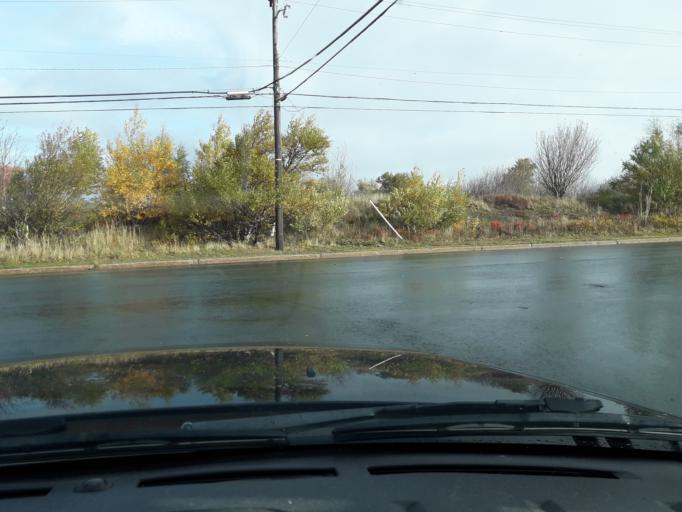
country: CA
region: Newfoundland and Labrador
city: St. John's
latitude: 47.5727
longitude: -52.6939
